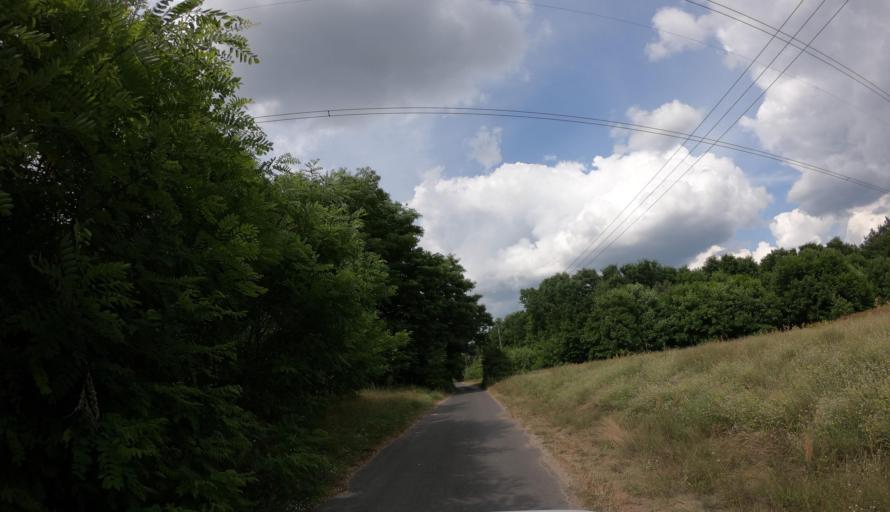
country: PL
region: West Pomeranian Voivodeship
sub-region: Powiat gryfinski
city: Stare Czarnowo
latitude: 53.3428
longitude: 14.7891
